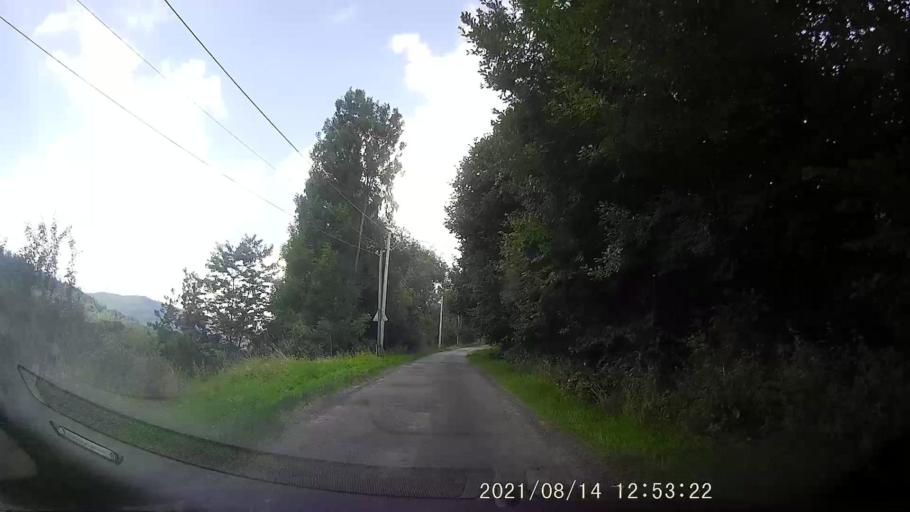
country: PL
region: Lower Silesian Voivodeship
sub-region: Powiat klodzki
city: Stronie Slaskie
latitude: 50.3207
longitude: 16.8267
